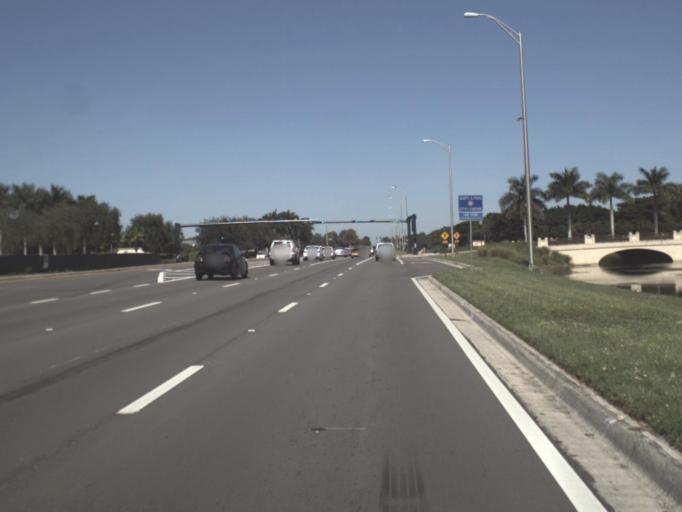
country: US
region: Florida
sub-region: Collier County
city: Naples
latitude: 26.1779
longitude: -81.7671
